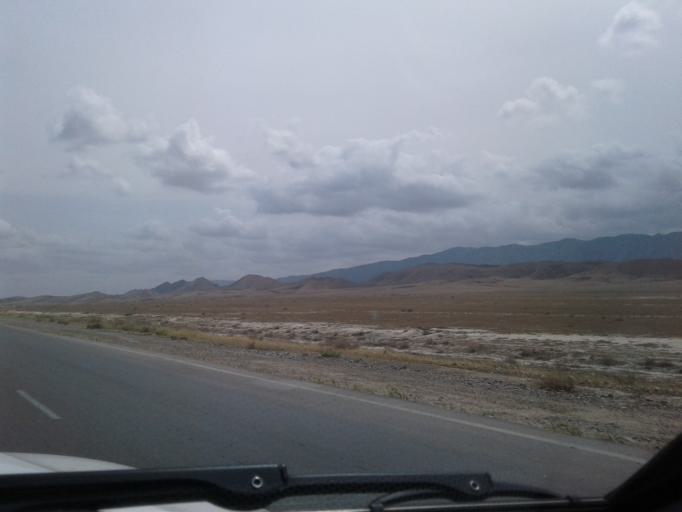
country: IR
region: Razavi Khorasan
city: Dargaz
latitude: 37.7074
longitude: 59.0316
